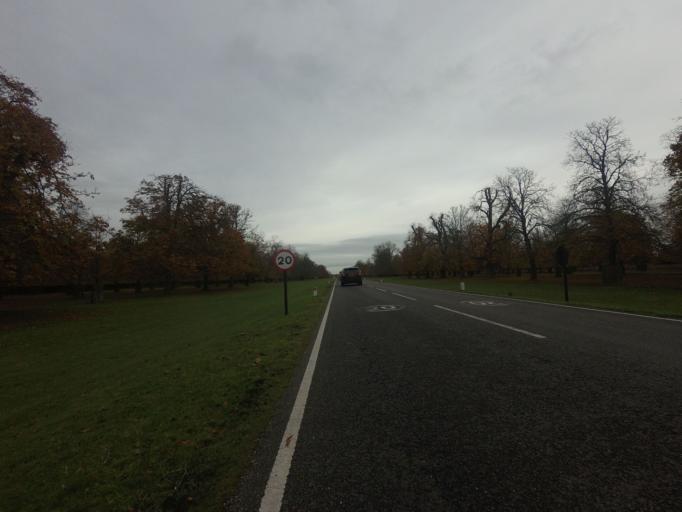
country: GB
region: England
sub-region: Greater London
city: Teddington
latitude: 51.4149
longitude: -0.3349
